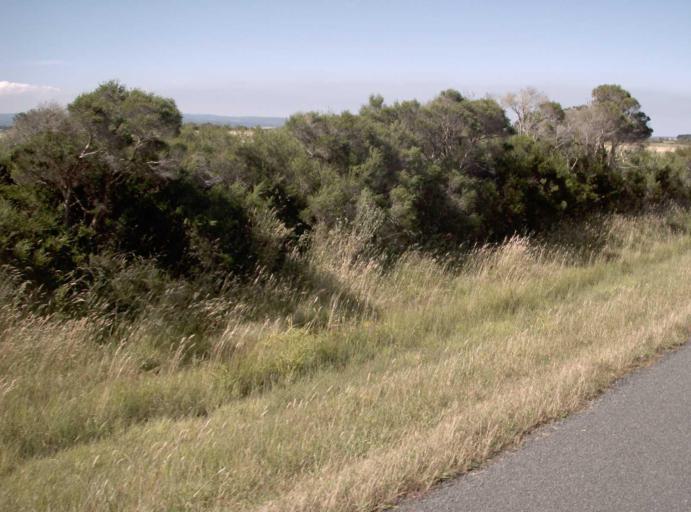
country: AU
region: Victoria
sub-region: Latrobe
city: Traralgon
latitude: -38.6335
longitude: 146.5870
